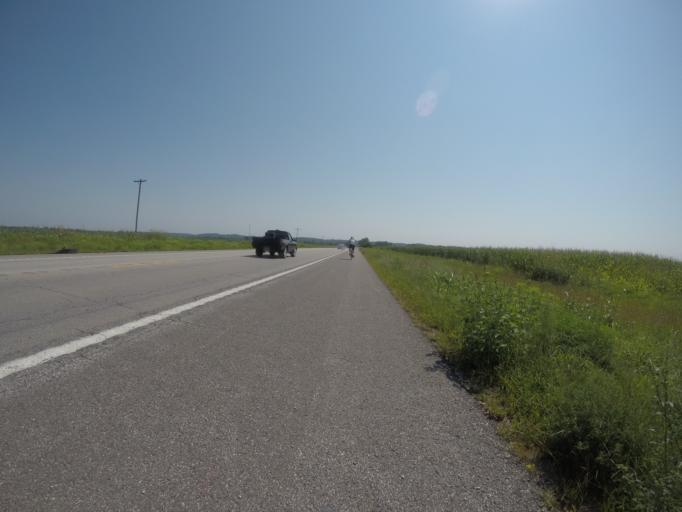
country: US
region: Kansas
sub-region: Atchison County
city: Atchison
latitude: 39.5572
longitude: -95.0906
